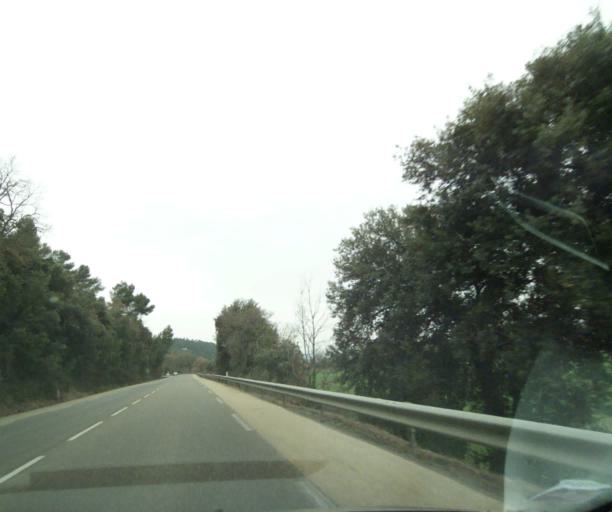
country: FR
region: Provence-Alpes-Cote d'Azur
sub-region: Departement des Bouches-du-Rhone
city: Jouques
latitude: 43.6616
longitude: 5.6390
